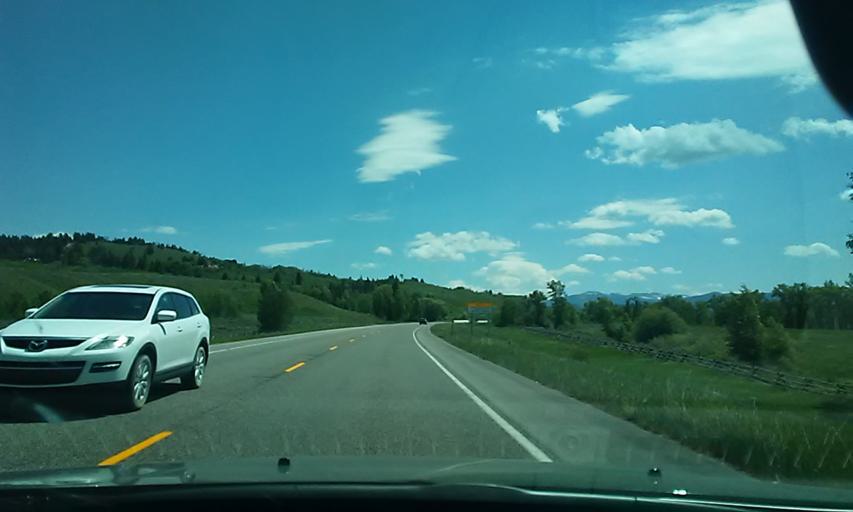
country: US
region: Wyoming
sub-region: Teton County
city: Jackson
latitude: 43.8398
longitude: -110.4632
